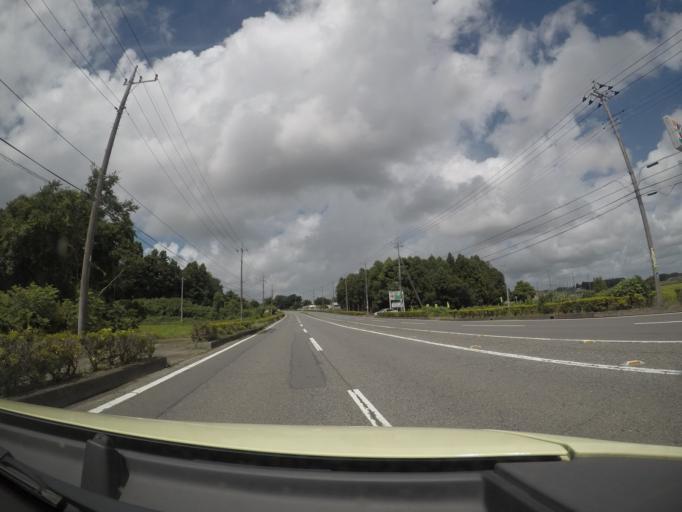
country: JP
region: Ibaraki
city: Mitsukaido
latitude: 36.0773
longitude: 140.0562
